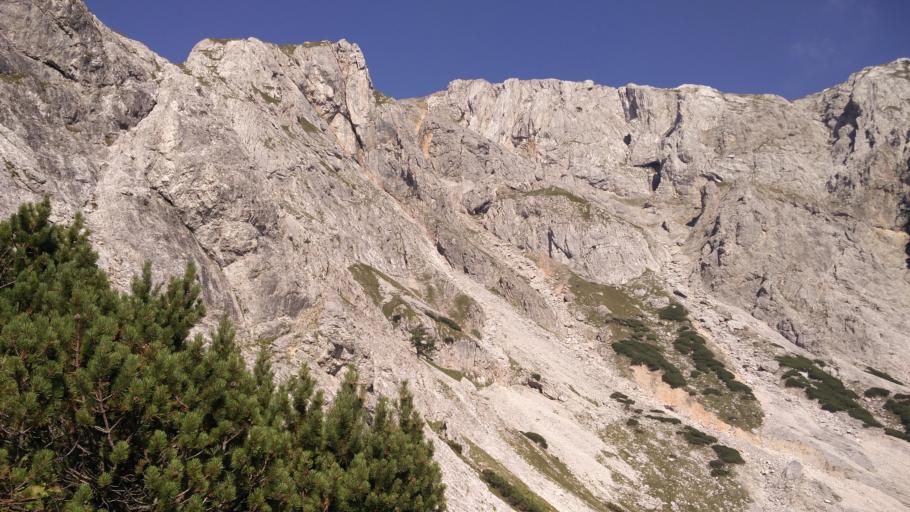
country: AT
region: Styria
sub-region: Politischer Bezirk Bruck-Muerzzuschlag
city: Sankt Ilgen
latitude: 47.6062
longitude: 15.1405
